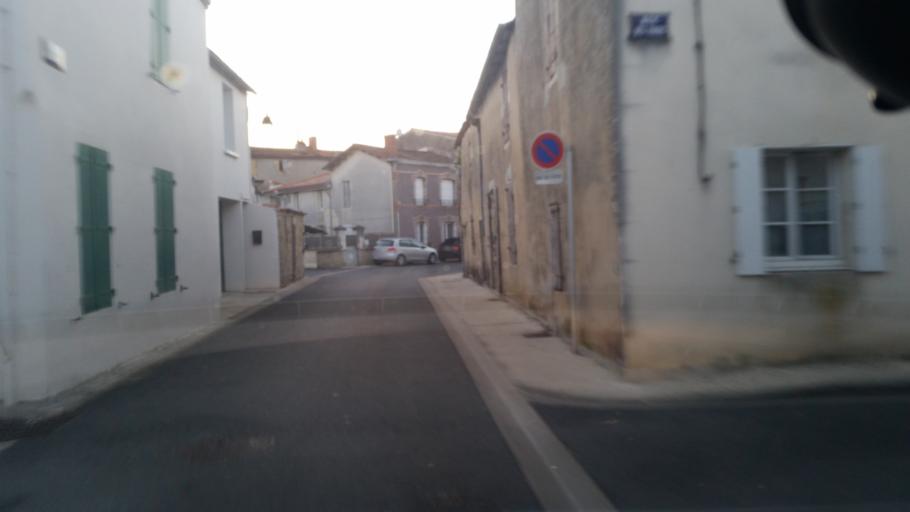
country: FR
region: Poitou-Charentes
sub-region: Departement de la Charente-Maritime
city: Marans
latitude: 46.3106
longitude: -0.9950
